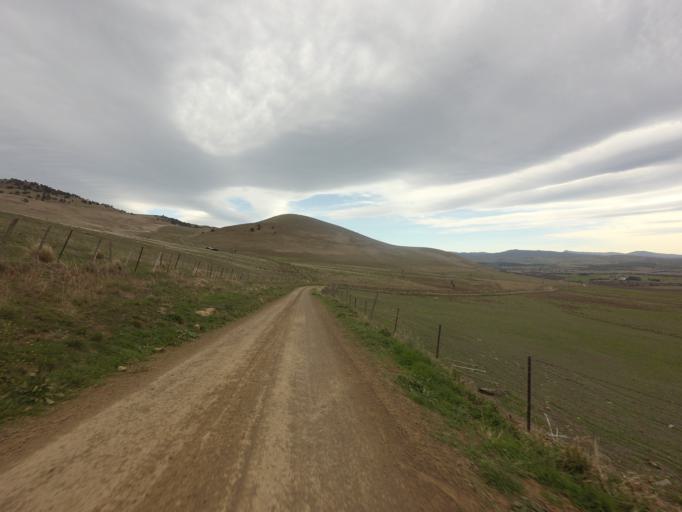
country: AU
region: Tasmania
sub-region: Derwent Valley
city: New Norfolk
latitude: -42.4582
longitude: 146.7617
